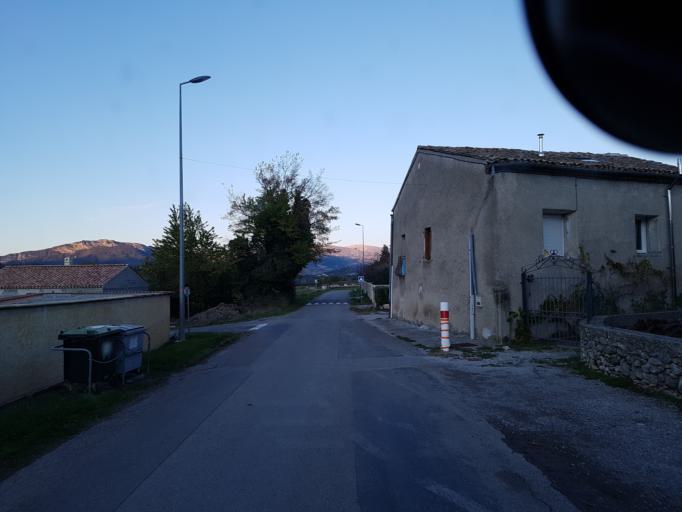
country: FR
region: Provence-Alpes-Cote d'Azur
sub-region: Departement des Alpes-de-Haute-Provence
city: Peipin
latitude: 44.1208
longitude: 5.9541
